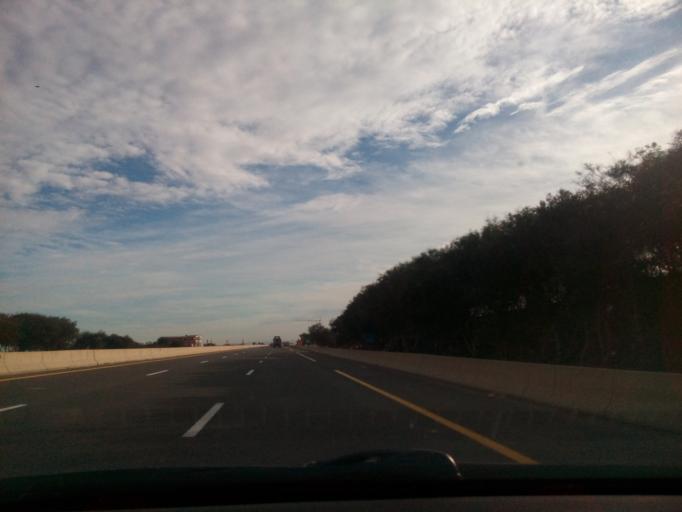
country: DZ
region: Mascara
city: Sig
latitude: 35.5418
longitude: -0.3601
